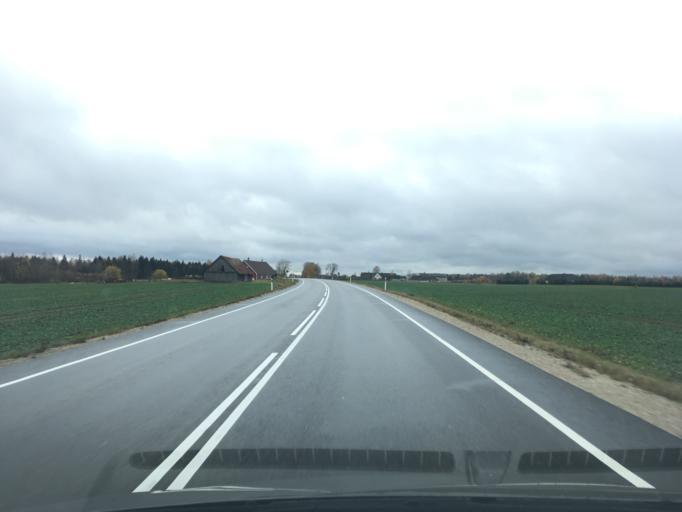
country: EE
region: Jogevamaa
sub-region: Tabivere vald
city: Tabivere
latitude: 58.4586
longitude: 26.5361
